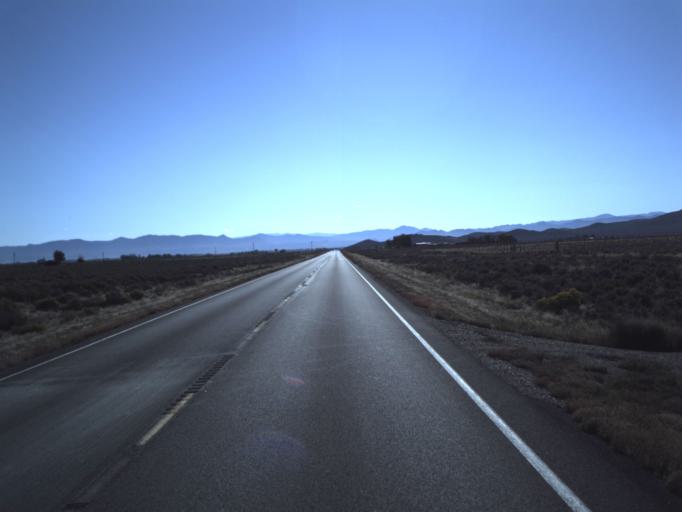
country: US
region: Utah
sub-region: Washington County
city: Enterprise
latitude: 37.7582
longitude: -113.7936
